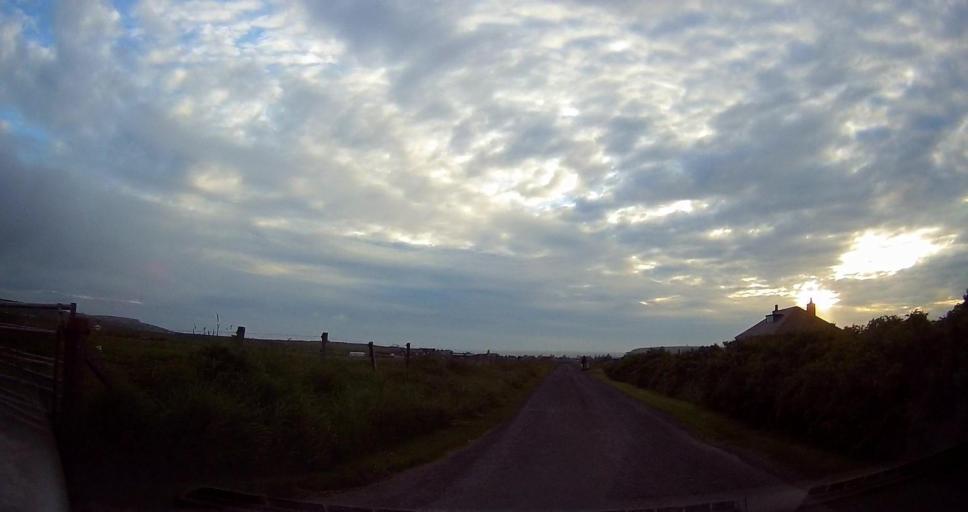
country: GB
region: Scotland
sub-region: Orkney Islands
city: Stromness
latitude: 59.1272
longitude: -3.2936
